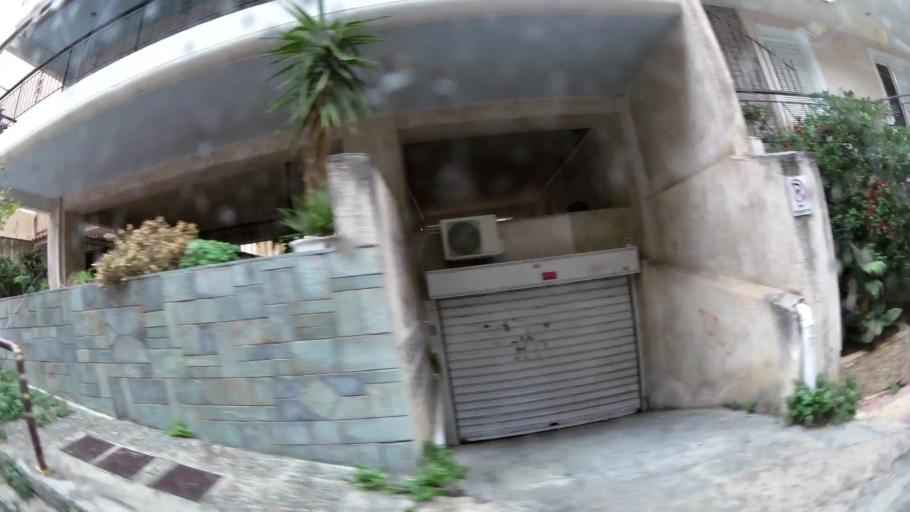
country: GR
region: Attica
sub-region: Nomarchia Athinas
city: Vyronas
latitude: 37.9589
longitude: 23.7509
